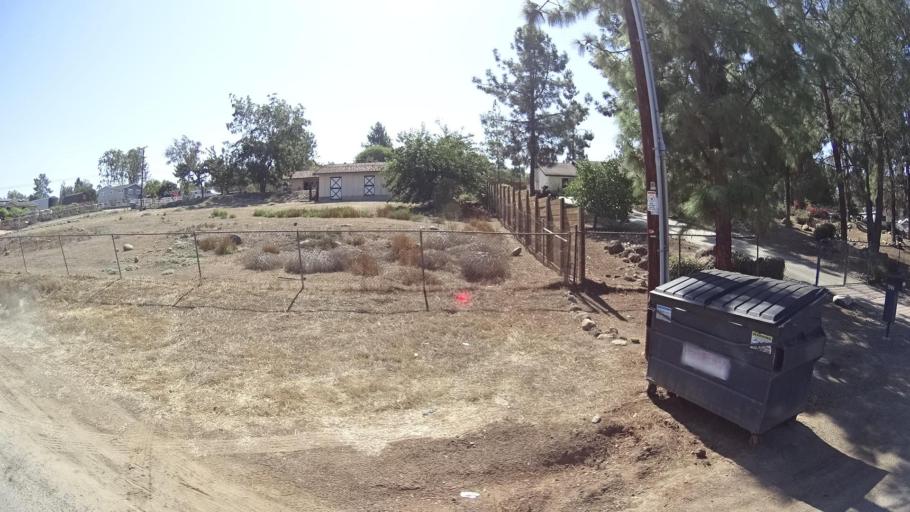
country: US
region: California
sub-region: San Diego County
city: Granite Hills
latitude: 32.7923
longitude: -116.9124
